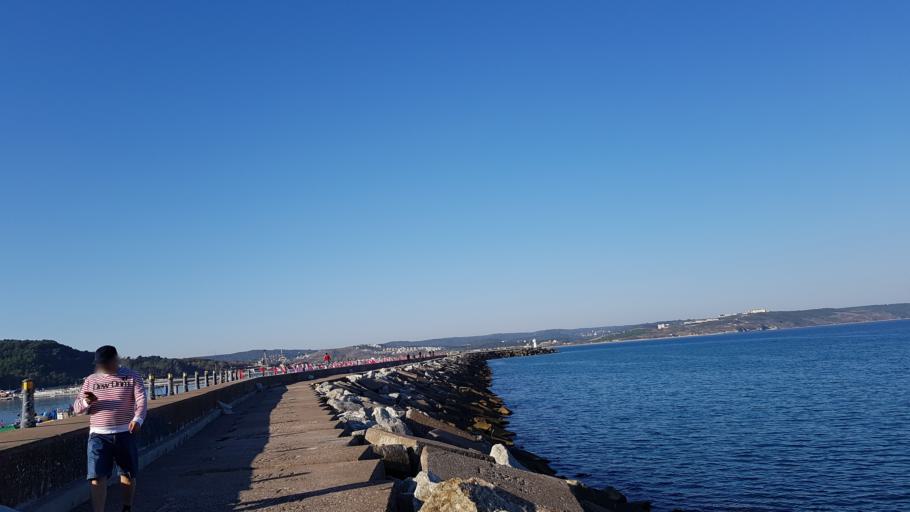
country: TR
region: Istanbul
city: Sile
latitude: 41.1816
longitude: 29.6065
